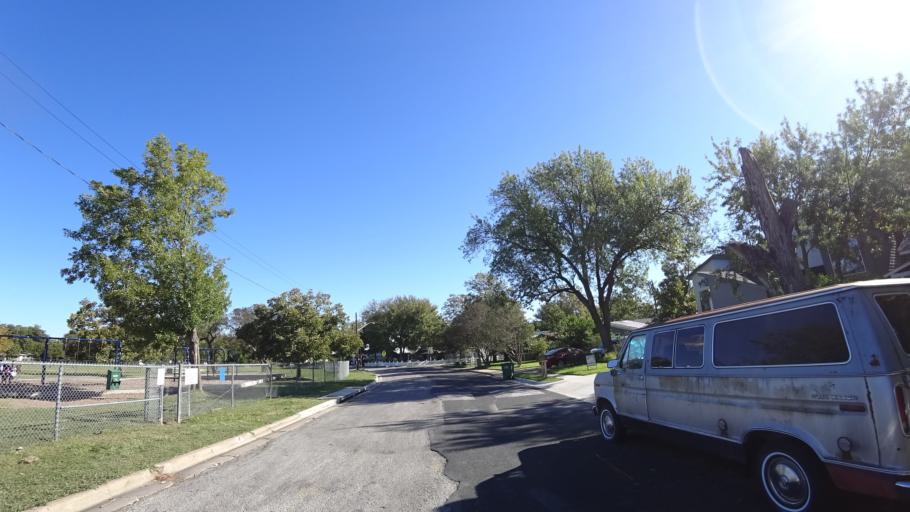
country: US
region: Texas
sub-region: Travis County
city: Austin
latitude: 30.2330
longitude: -97.7628
